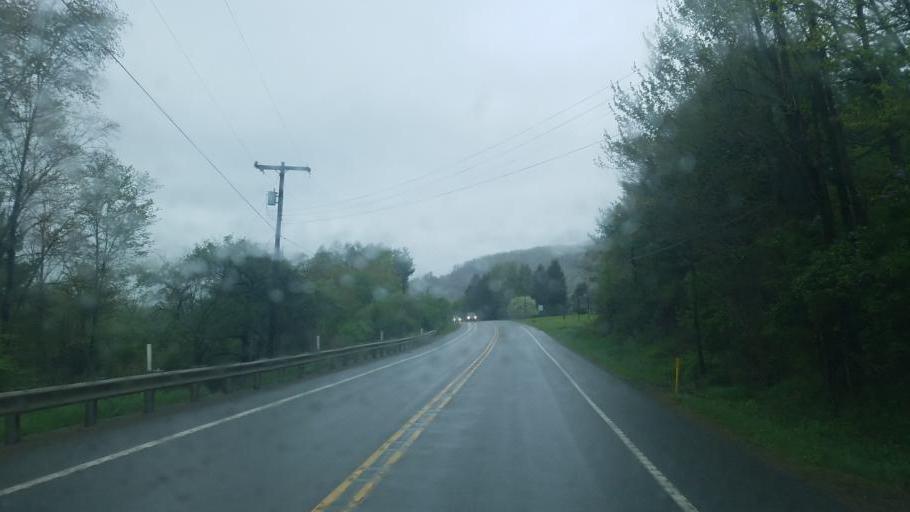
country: US
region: Pennsylvania
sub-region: Potter County
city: Coudersport
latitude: 41.7573
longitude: -78.1104
